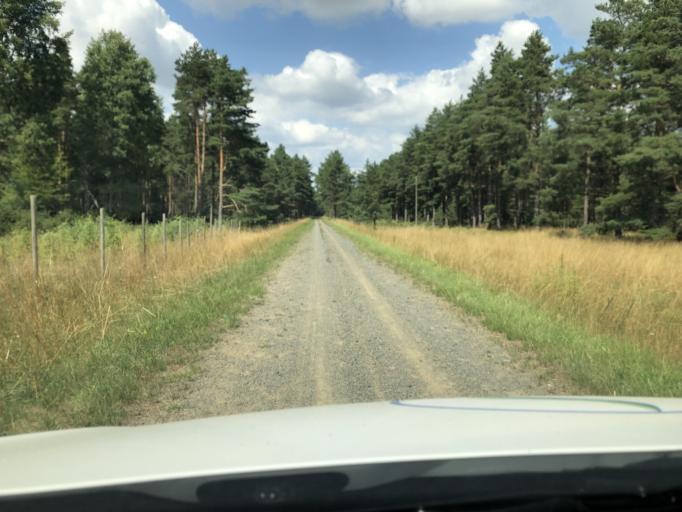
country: SE
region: Skane
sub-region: Kristianstads Kommun
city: Degeberga
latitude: 55.8679
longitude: 14.0806
